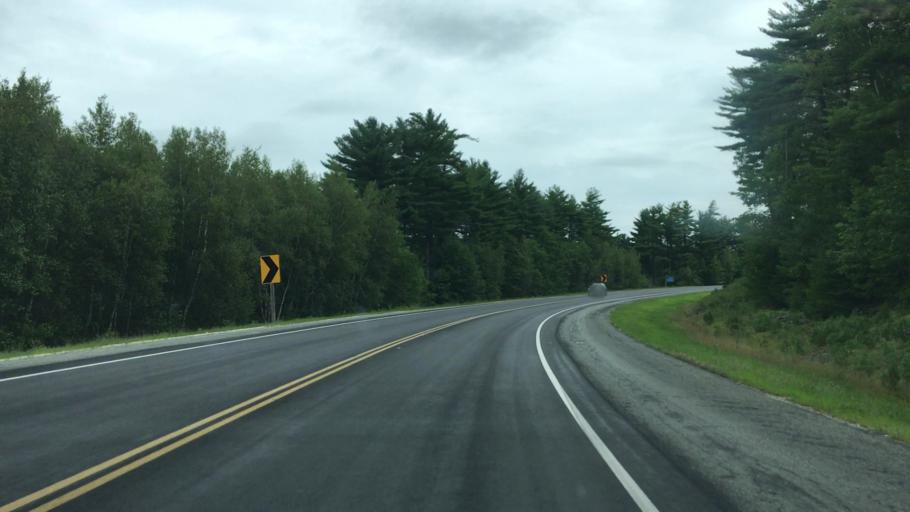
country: US
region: Maine
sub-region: Washington County
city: Cherryfield
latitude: 44.9094
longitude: -67.8563
